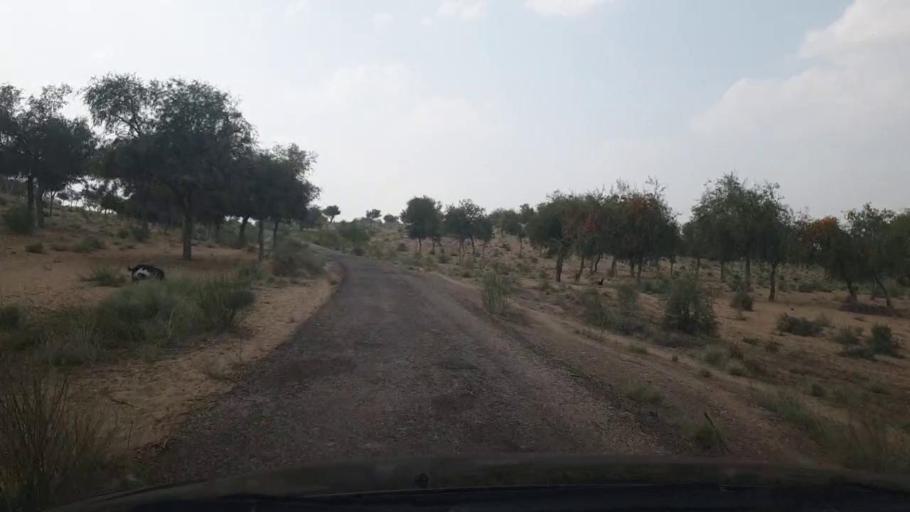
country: PK
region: Sindh
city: Islamkot
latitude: 24.9680
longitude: 70.6003
